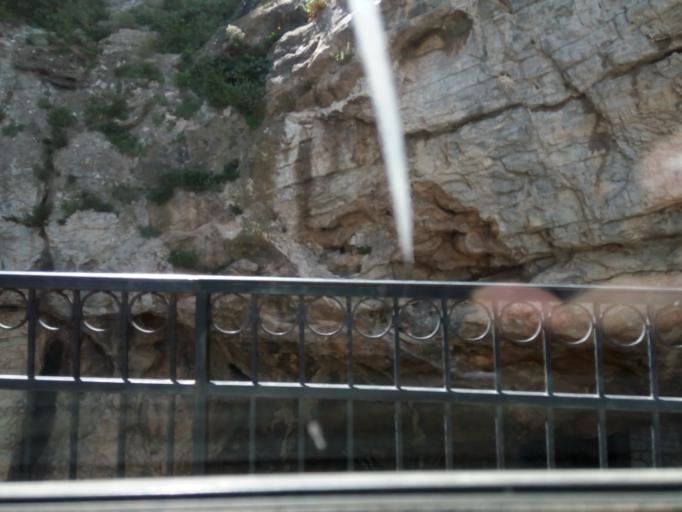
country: DZ
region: Constantine
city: Constantine
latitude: 36.3720
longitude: 6.6121
